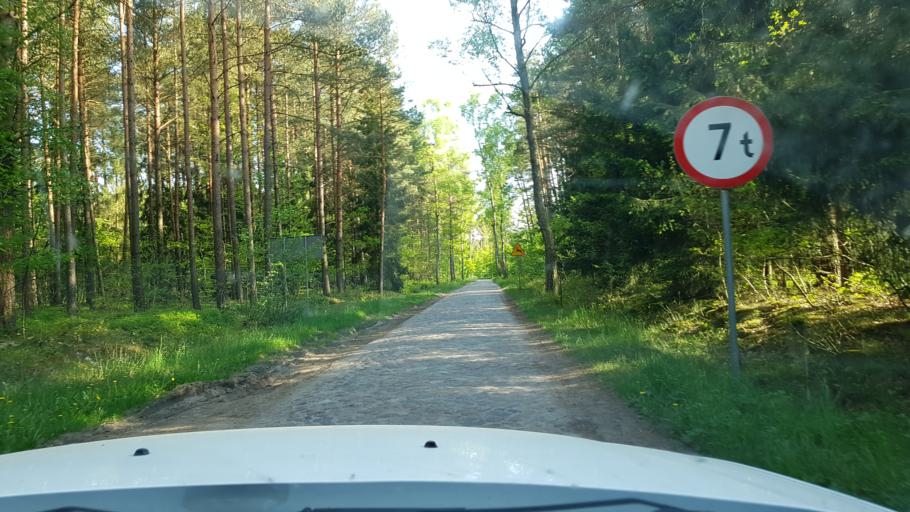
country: PL
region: West Pomeranian Voivodeship
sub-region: Powiat lobeski
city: Resko
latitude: 53.7289
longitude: 15.3254
